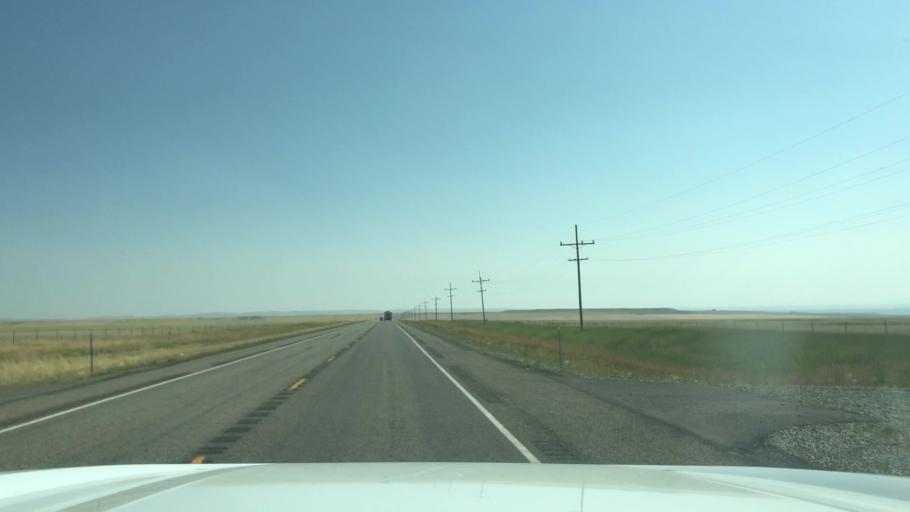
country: US
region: Montana
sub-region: Wheatland County
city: Harlowton
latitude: 46.5047
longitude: -109.7661
